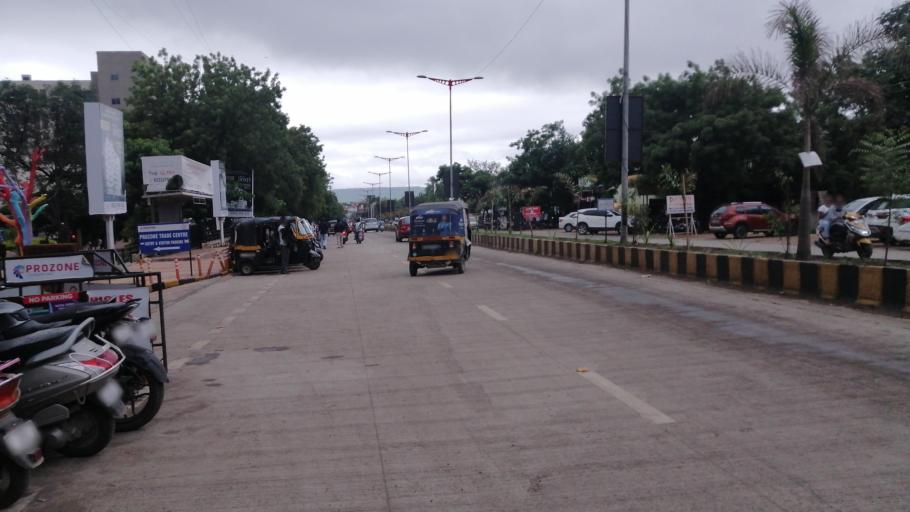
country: IN
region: Maharashtra
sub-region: Aurangabad Division
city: Aurangabad
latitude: 19.8779
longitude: 75.3712
